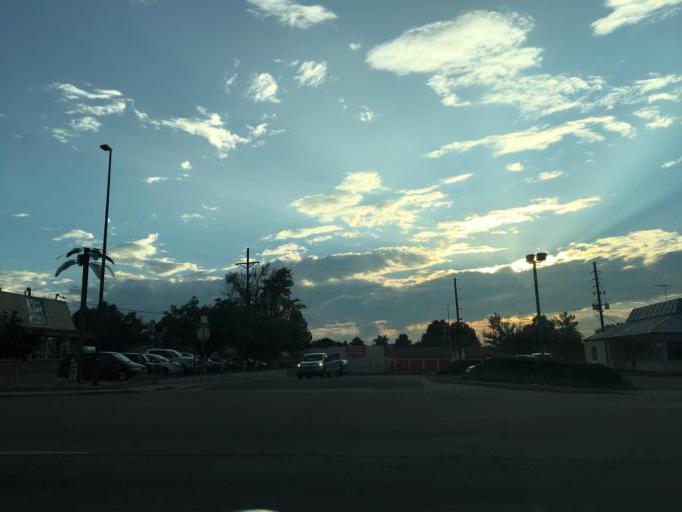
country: US
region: Colorado
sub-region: Adams County
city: Aurora
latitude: 39.7240
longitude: -104.8658
